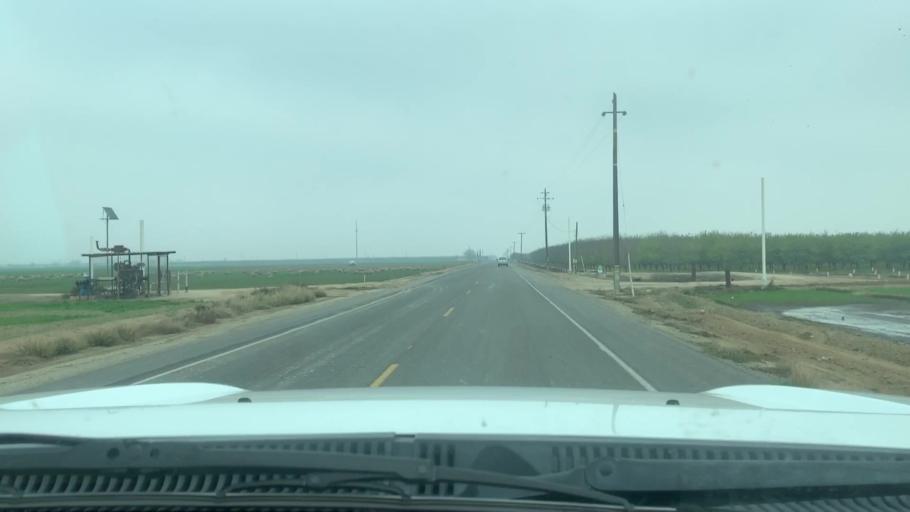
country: US
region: California
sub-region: Kern County
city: Wasco
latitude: 35.5001
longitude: -119.3773
